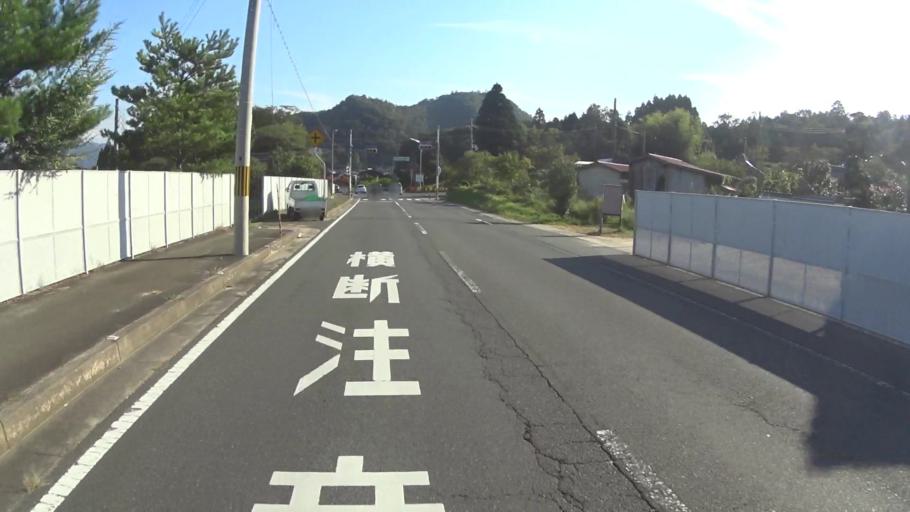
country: JP
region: Hyogo
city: Toyooka
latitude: 35.6130
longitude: 134.9191
